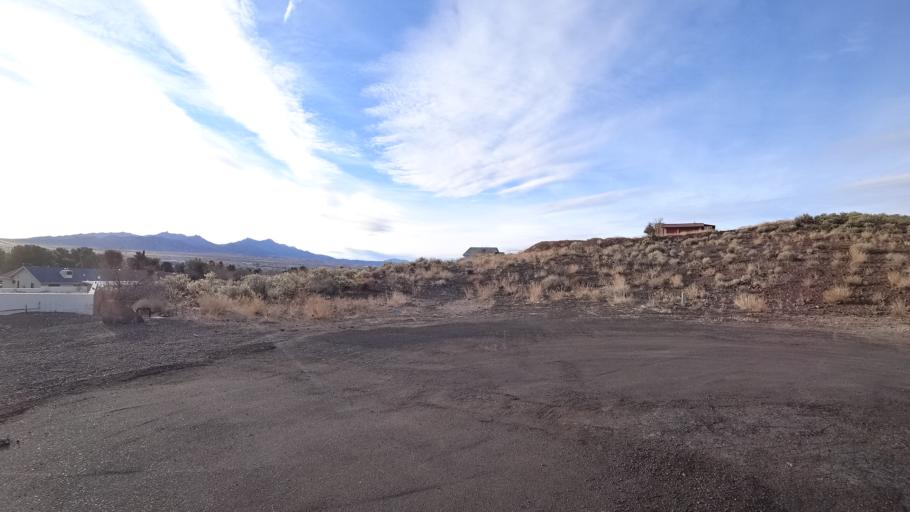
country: US
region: Arizona
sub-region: Mohave County
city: New Kingman-Butler
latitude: 35.2412
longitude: -114.0439
